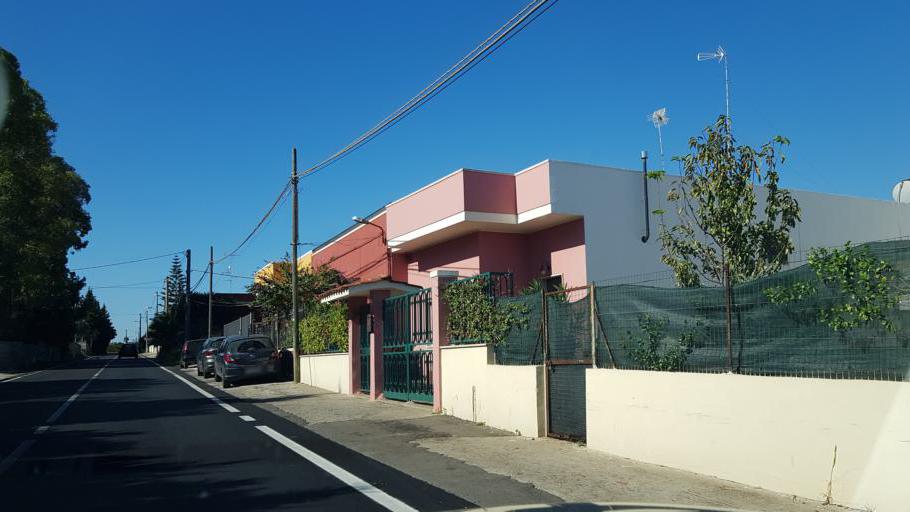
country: IT
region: Apulia
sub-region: Provincia di Lecce
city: Arnesano
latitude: 40.3281
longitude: 18.0833
